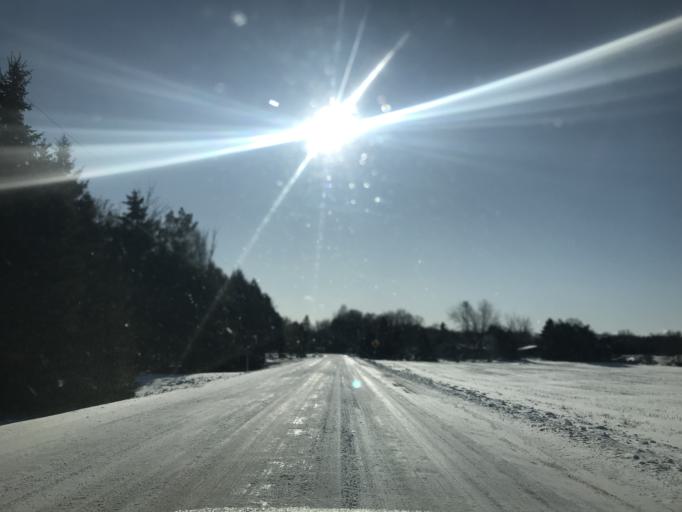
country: US
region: Wisconsin
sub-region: Door County
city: Sturgeon Bay
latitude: 44.8258
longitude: -87.5041
